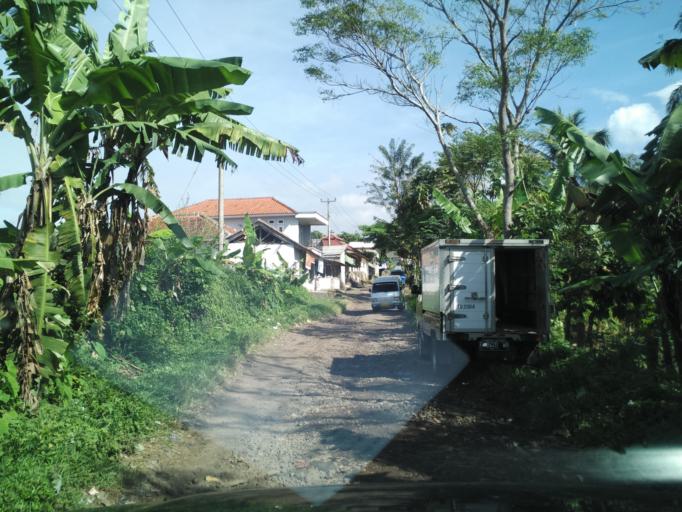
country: ID
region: West Java
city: Sukabumi
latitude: -6.8483
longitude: 107.0600
